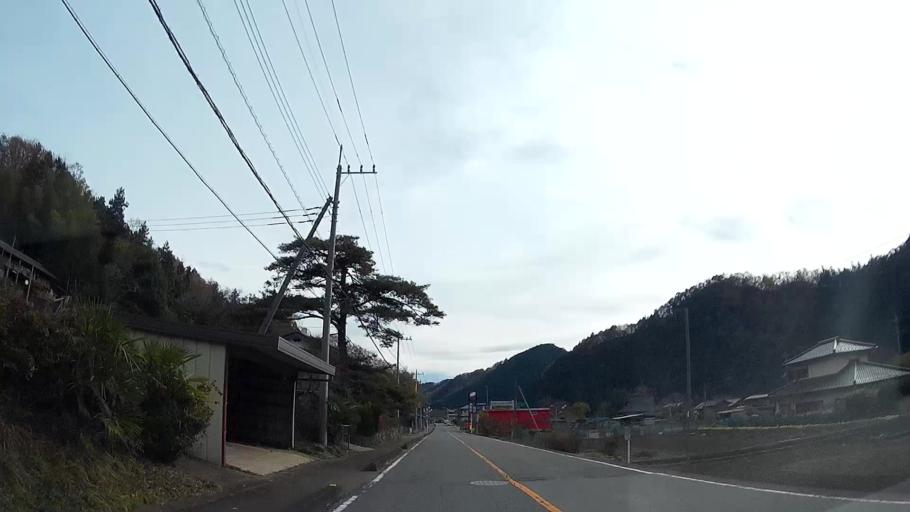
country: JP
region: Saitama
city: Chichibu
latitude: 36.0483
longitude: 138.9830
